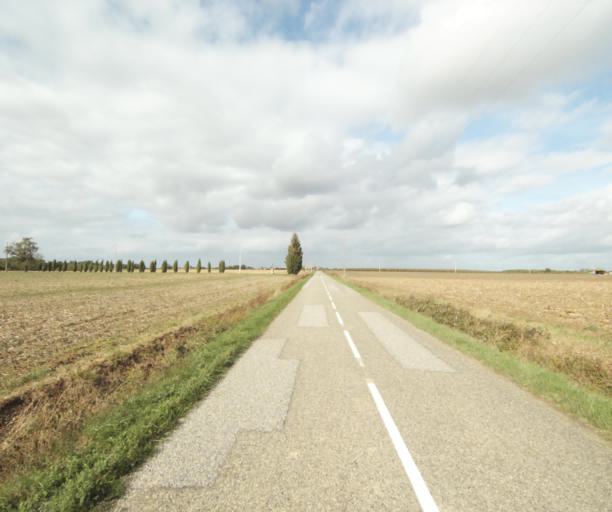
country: FR
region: Midi-Pyrenees
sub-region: Departement du Tarn-et-Garonne
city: Finhan
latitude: 43.9043
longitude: 1.1465
